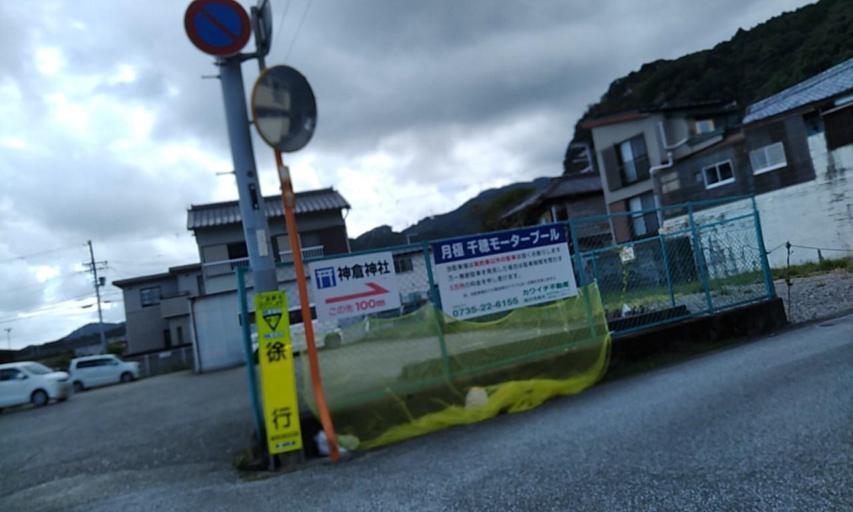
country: JP
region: Wakayama
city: Shingu
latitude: 33.7244
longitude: 135.9855
